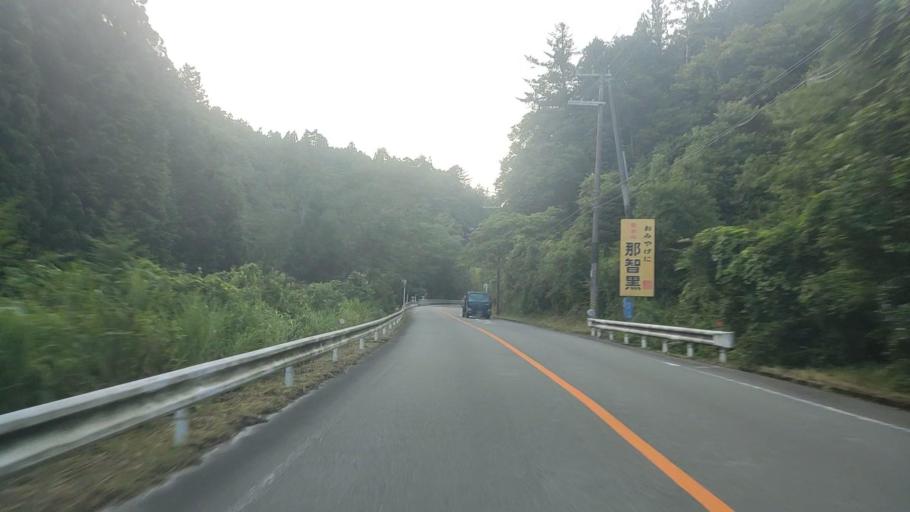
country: JP
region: Wakayama
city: Tanabe
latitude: 33.8147
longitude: 135.6161
